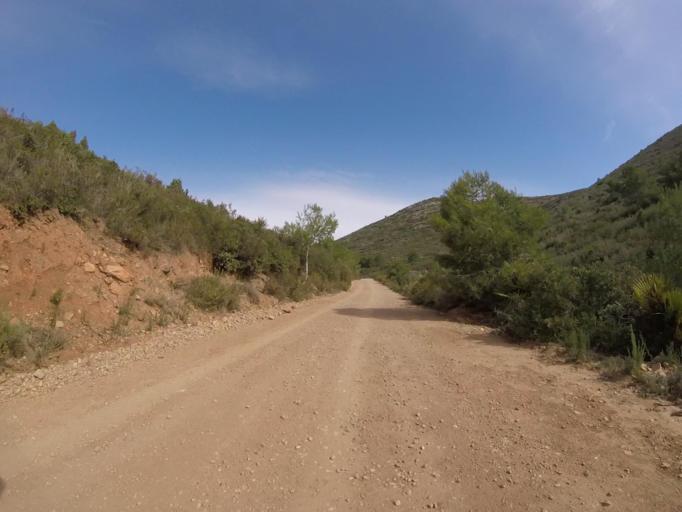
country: ES
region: Valencia
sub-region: Provincia de Castello
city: Torreblanca
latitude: 40.1997
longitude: 0.1539
